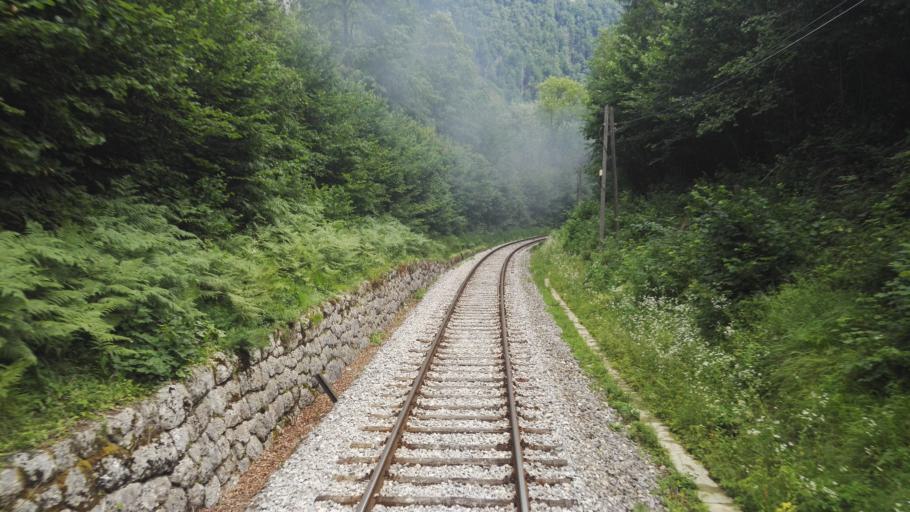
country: SI
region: Bohinj
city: Bohinjska Bistrica
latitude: 46.2961
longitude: 14.0352
